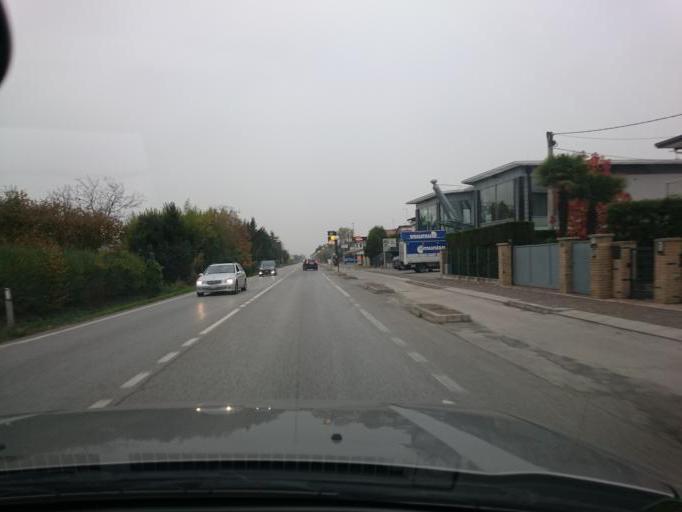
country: IT
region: Veneto
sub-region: Provincia di Padova
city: Sant'Angelo di Piove di Sacco
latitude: 45.3221
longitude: 11.9983
